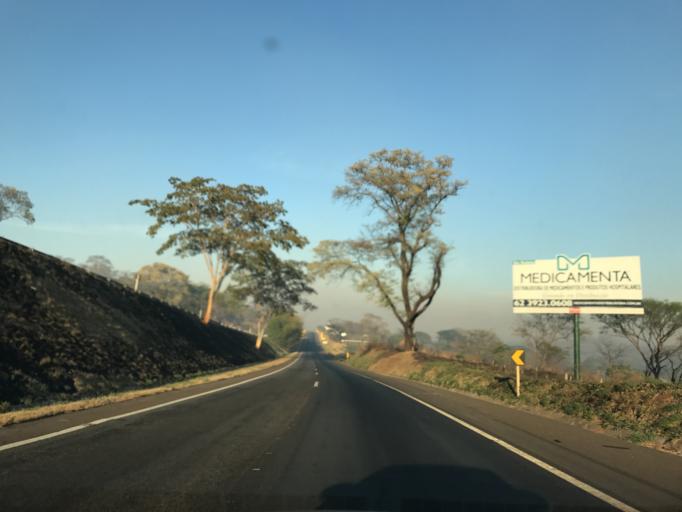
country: BR
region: Goias
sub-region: Goiania
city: Goiania
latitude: -16.5815
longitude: -49.1851
